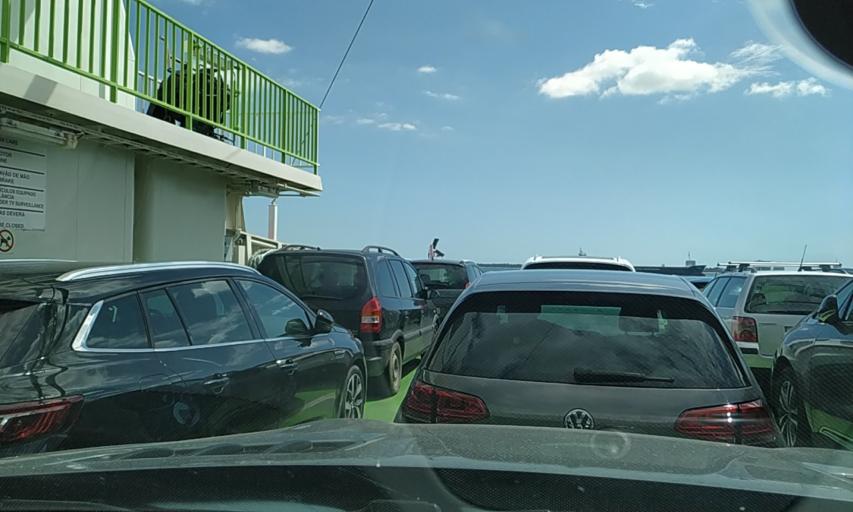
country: PT
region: Setubal
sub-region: Setubal
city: Setubal
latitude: 38.5199
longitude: -8.8857
